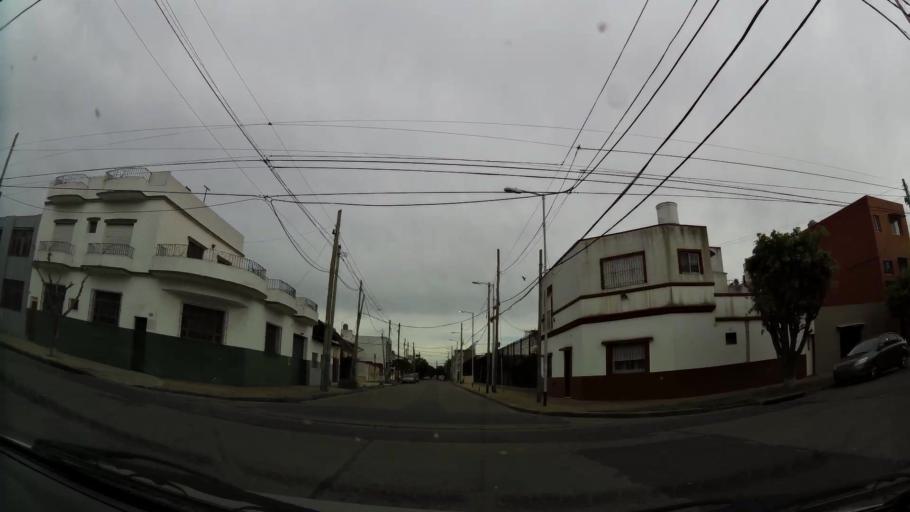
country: AR
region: Buenos Aires
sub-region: Partido de Avellaneda
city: Avellaneda
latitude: -34.6715
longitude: -58.3495
